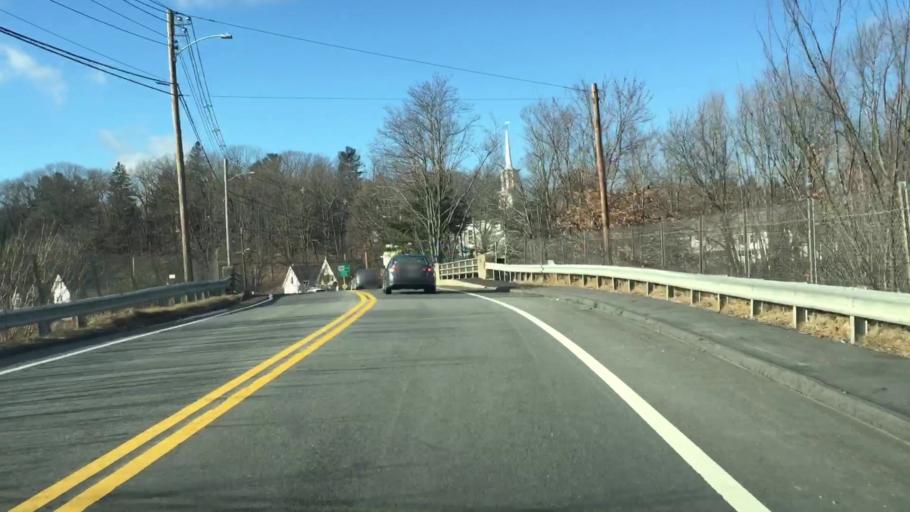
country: US
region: Massachusetts
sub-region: Worcester County
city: West Boylston
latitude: 42.3882
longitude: -71.7920
